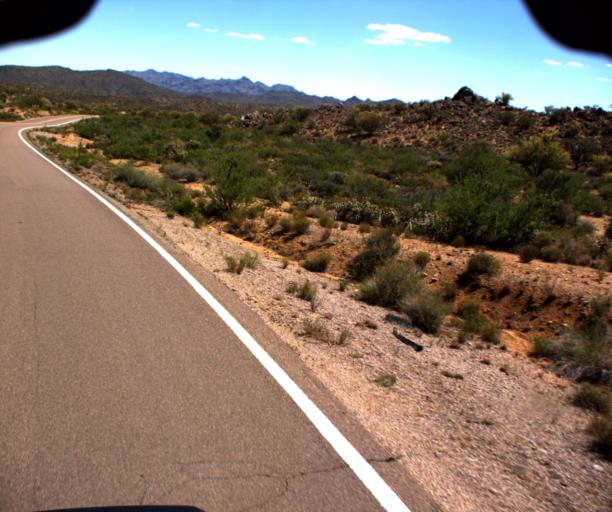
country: US
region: Arizona
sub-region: Yavapai County
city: Bagdad
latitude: 34.4591
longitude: -113.2440
